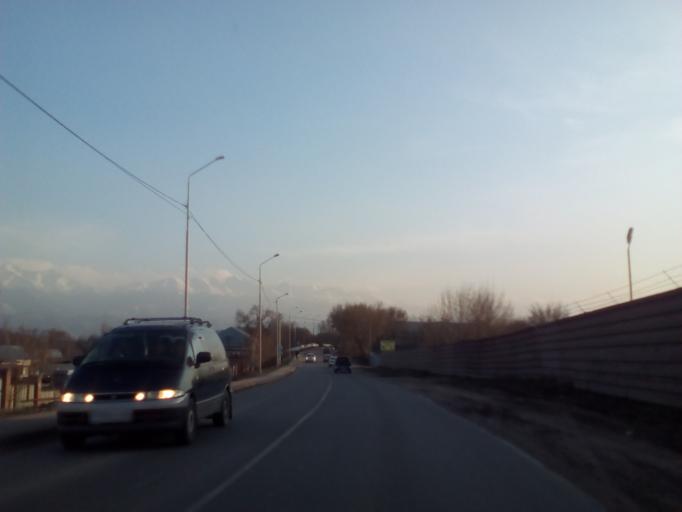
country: KZ
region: Almaty Oblysy
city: Burunday
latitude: 43.2506
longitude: 76.7631
